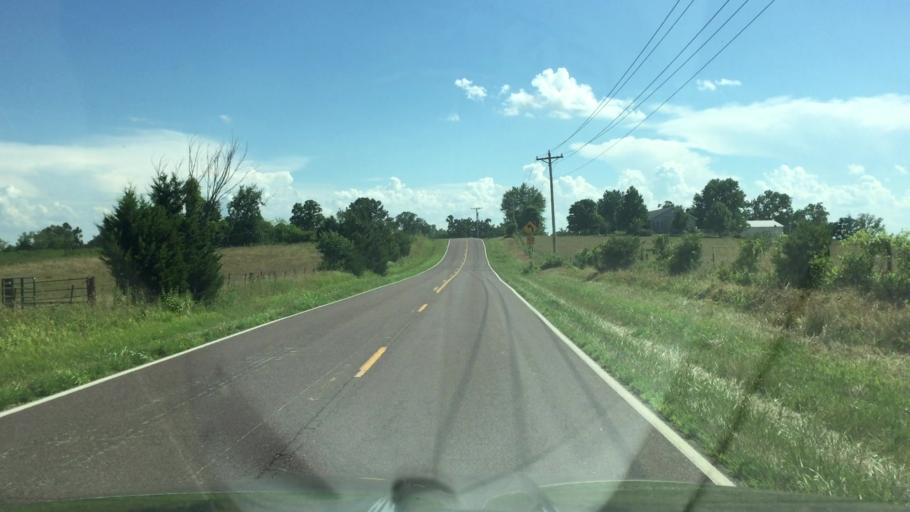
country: US
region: Missouri
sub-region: Miller County
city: Tuscumbia
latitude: 38.0982
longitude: -92.4787
